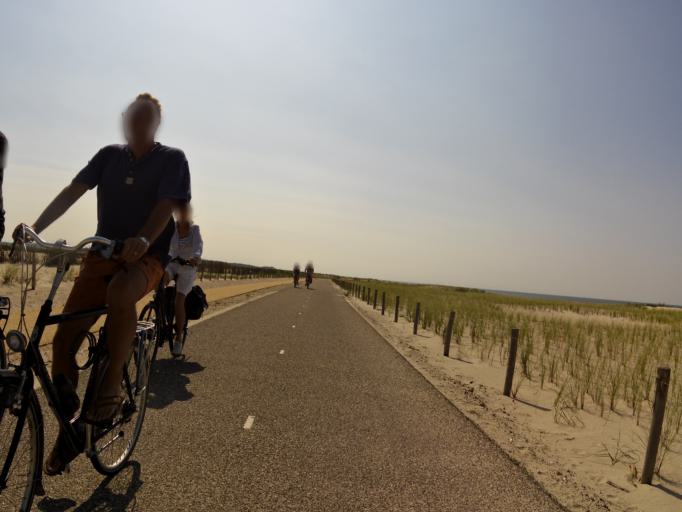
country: NL
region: North Holland
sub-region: Gemeente Schagen
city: Harenkarspel
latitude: 52.7651
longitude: 4.6530
